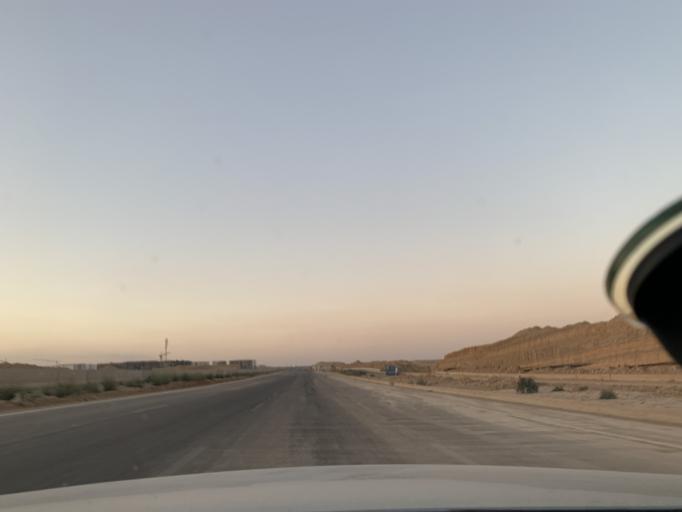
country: EG
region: Muhafazat al Qahirah
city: Halwan
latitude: 29.9589
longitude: 31.5444
